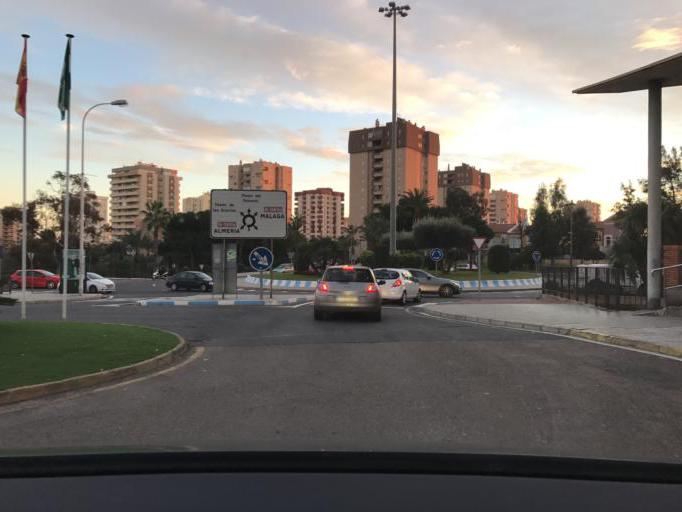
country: ES
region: Andalusia
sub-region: Provincia de Almeria
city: Aguadulce
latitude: 36.8133
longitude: -2.5786
